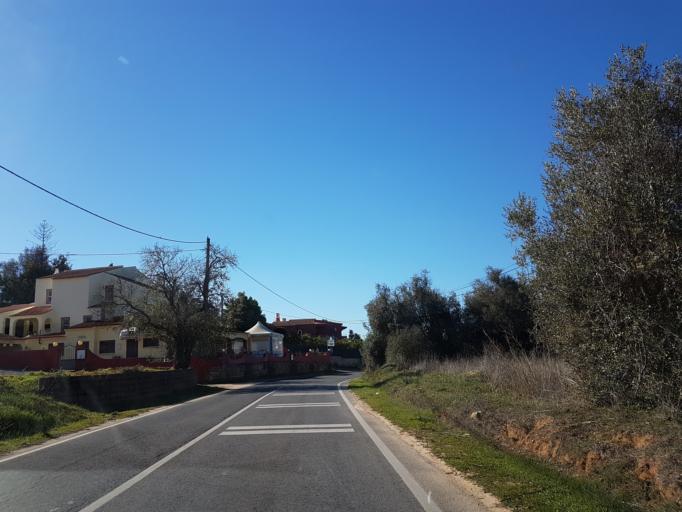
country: PT
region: Faro
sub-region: Lagoa
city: Carvoeiro
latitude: 37.1125
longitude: -8.4522
